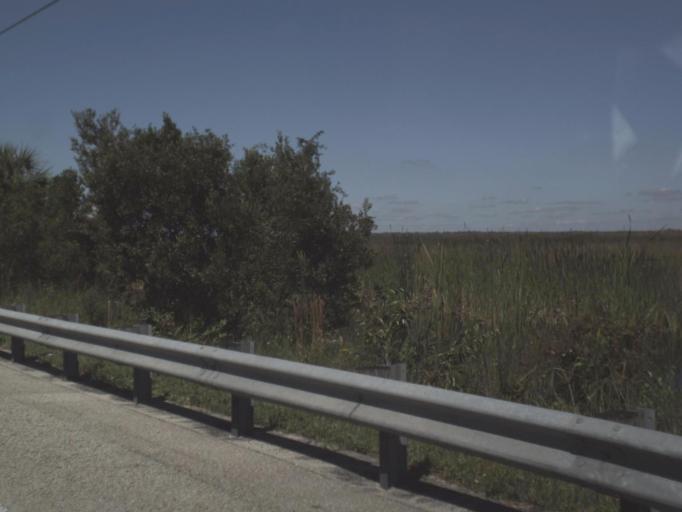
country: US
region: Florida
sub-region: Collier County
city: Marco
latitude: 25.9187
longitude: -81.3922
